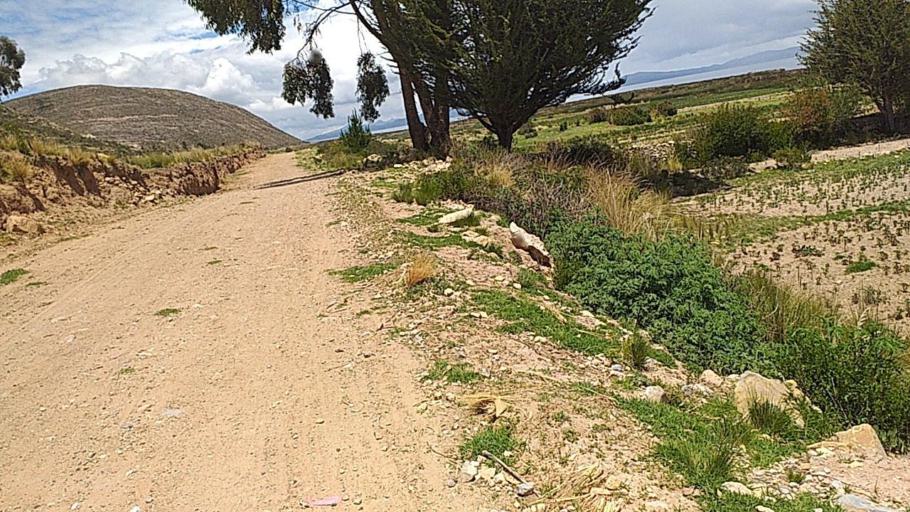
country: BO
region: La Paz
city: Huatajata
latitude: -16.3091
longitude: -68.6817
